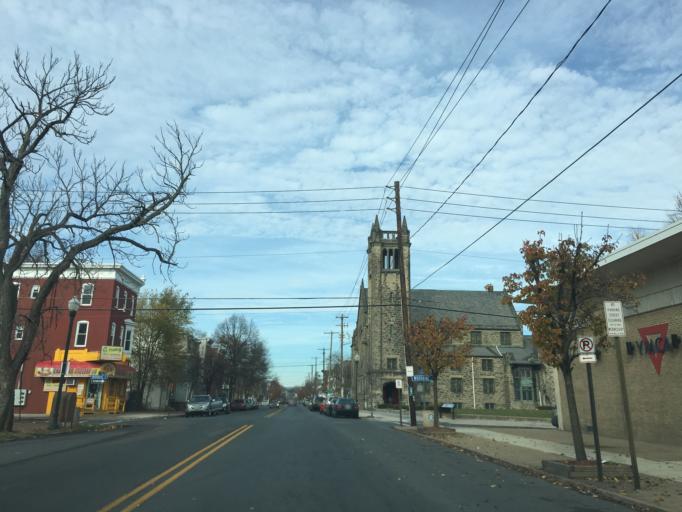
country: US
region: Pennsylvania
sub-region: Dauphin County
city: Harrisburg
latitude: 40.2818
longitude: -76.8911
